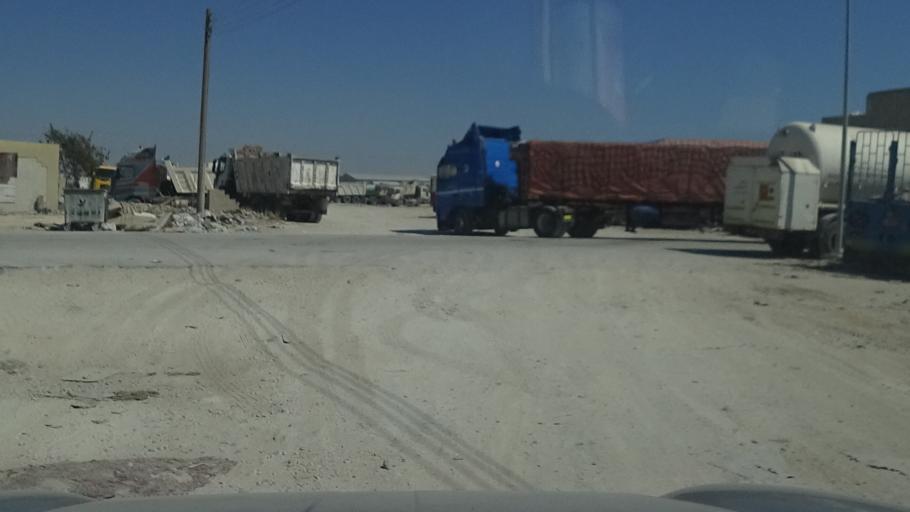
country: OM
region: Zufar
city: Salalah
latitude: 17.0317
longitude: 54.0431
